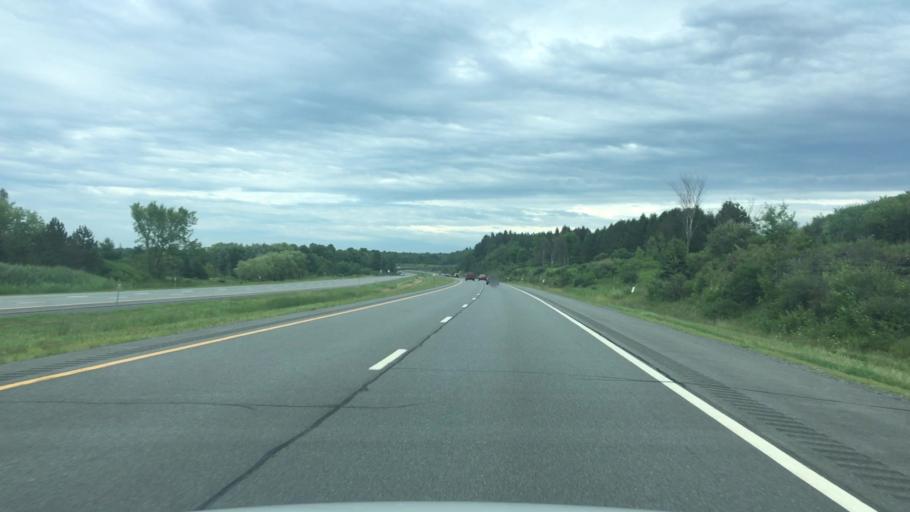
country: US
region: New York
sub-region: Schoharie County
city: Schoharie
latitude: 42.7281
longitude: -74.1959
